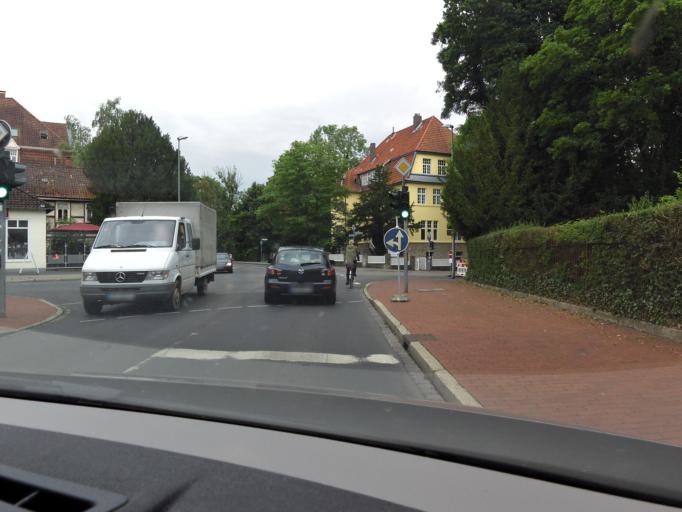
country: DE
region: Lower Saxony
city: Goettingen
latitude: 51.5350
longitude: 9.9448
